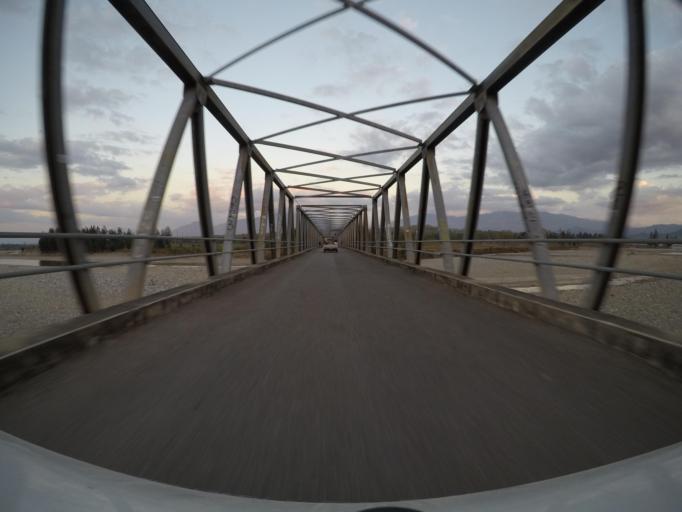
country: TL
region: Bobonaro
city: Maliana
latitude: -8.9609
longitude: 125.1118
